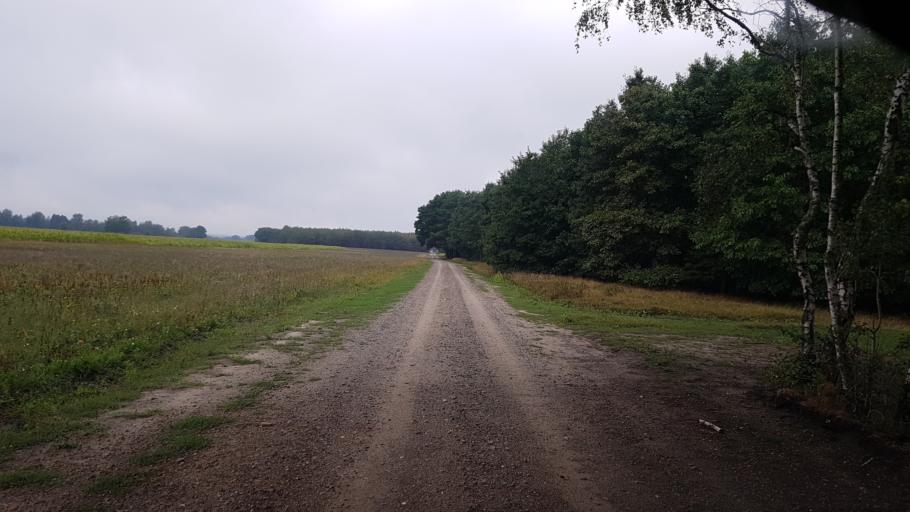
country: DE
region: Brandenburg
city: Ruckersdorf
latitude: 51.5574
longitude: 13.5670
